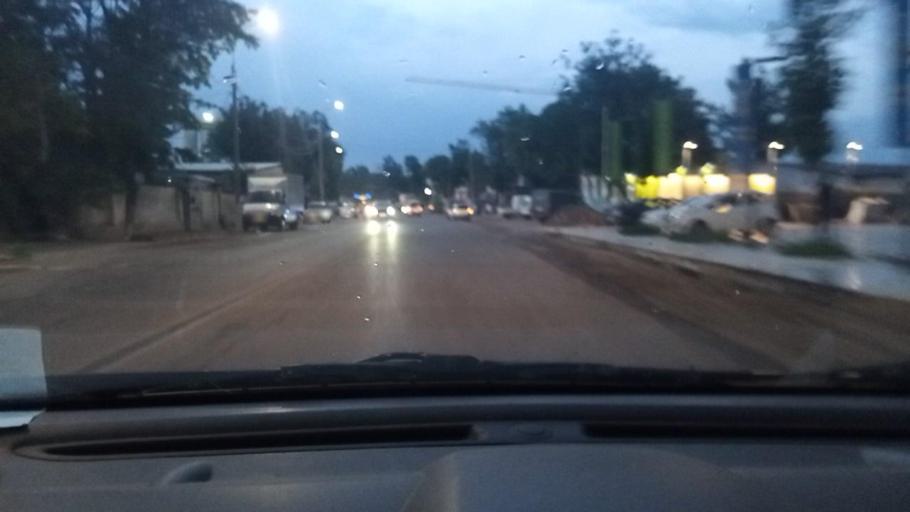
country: UZ
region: Toshkent
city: Salor
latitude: 41.3136
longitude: 69.3329
